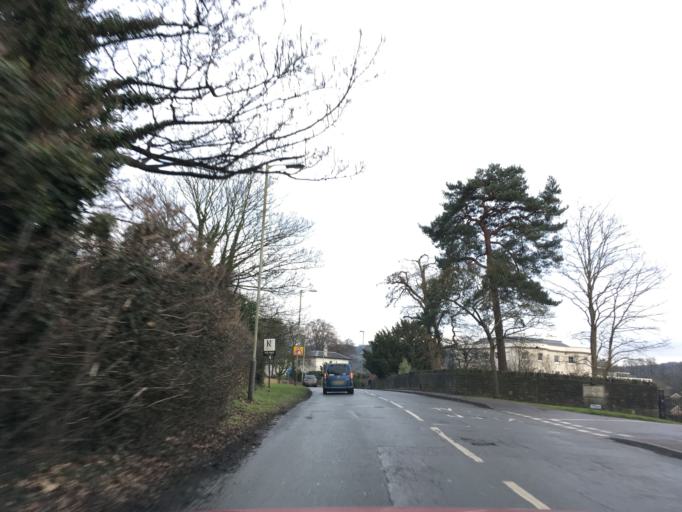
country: GB
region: England
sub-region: Gloucestershire
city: Charlton Kings
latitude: 51.8894
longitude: -2.0588
